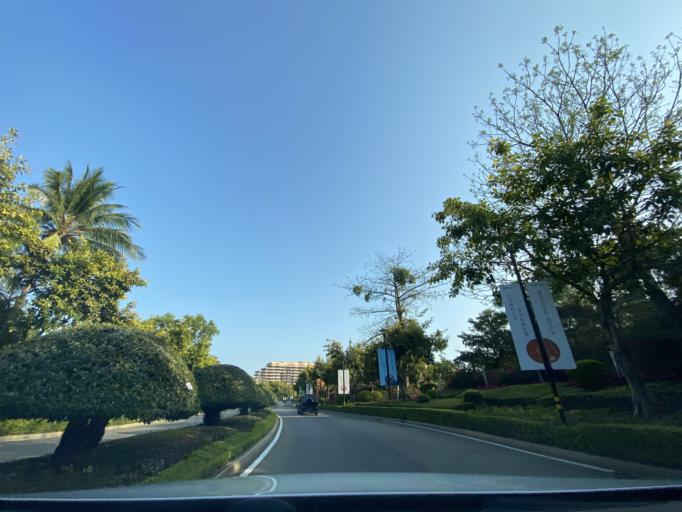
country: CN
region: Hainan
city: Yingzhou
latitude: 18.3963
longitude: 109.8556
